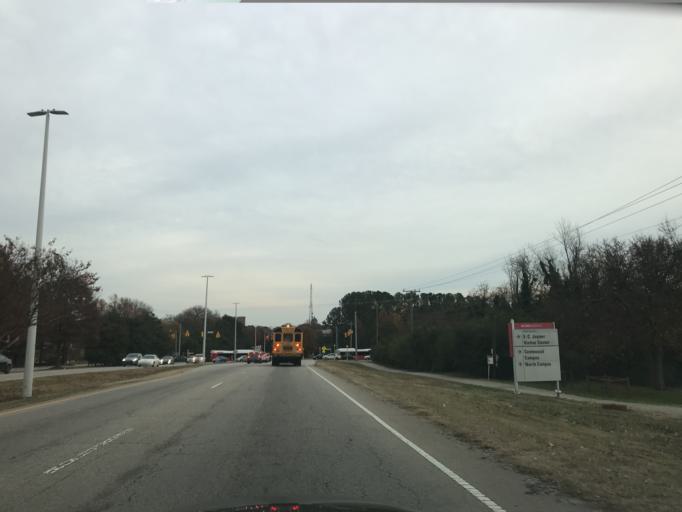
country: US
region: North Carolina
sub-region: Wake County
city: West Raleigh
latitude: 35.7843
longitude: -78.6839
